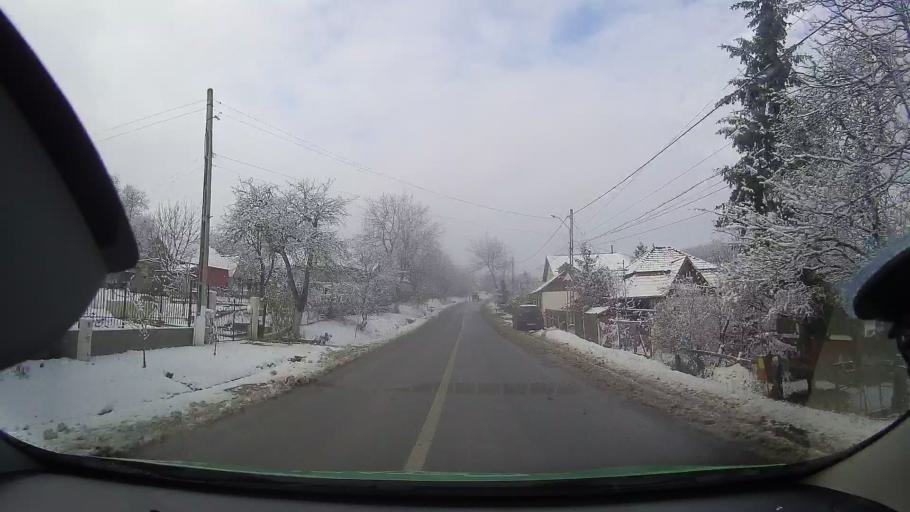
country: RO
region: Mures
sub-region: Comuna Atintis
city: Atintis
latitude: 46.4330
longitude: 24.1001
